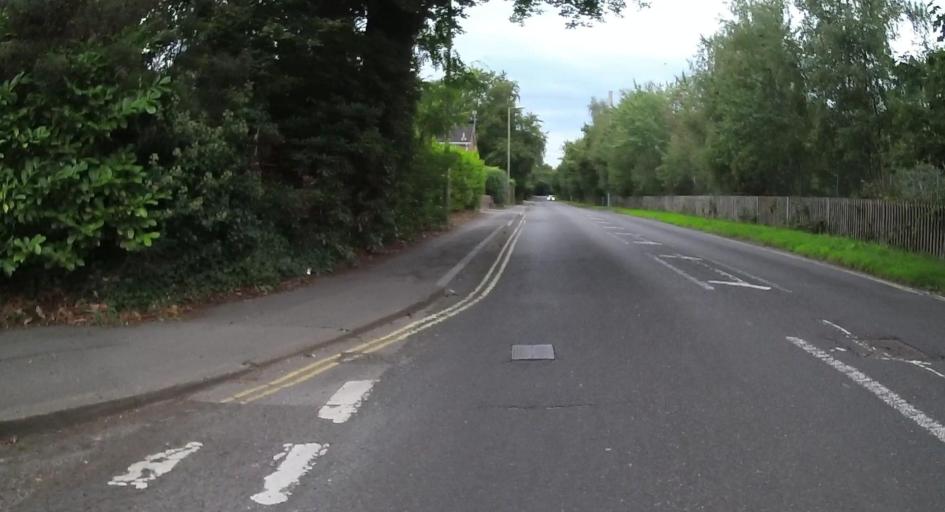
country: GB
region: England
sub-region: Hampshire
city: Fleet
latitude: 51.2901
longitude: -0.8355
